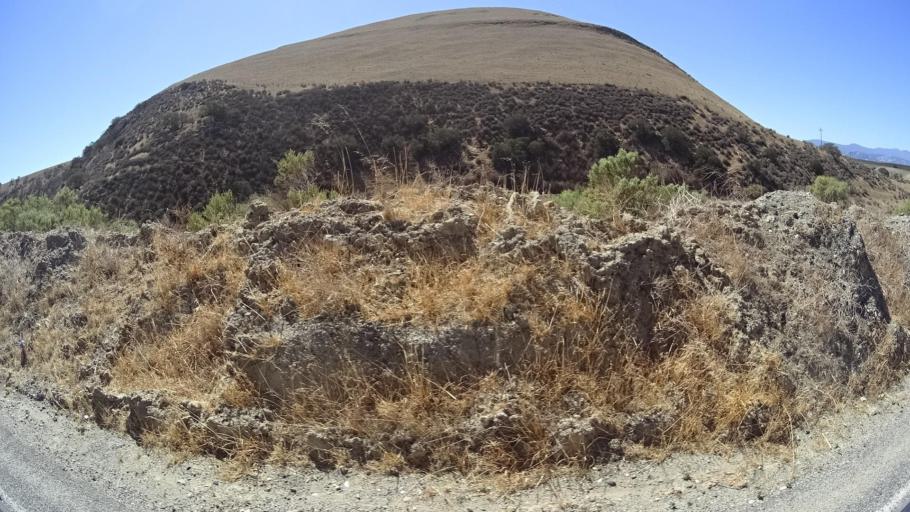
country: US
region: California
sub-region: Monterey County
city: King City
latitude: 36.2682
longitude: -121.0708
